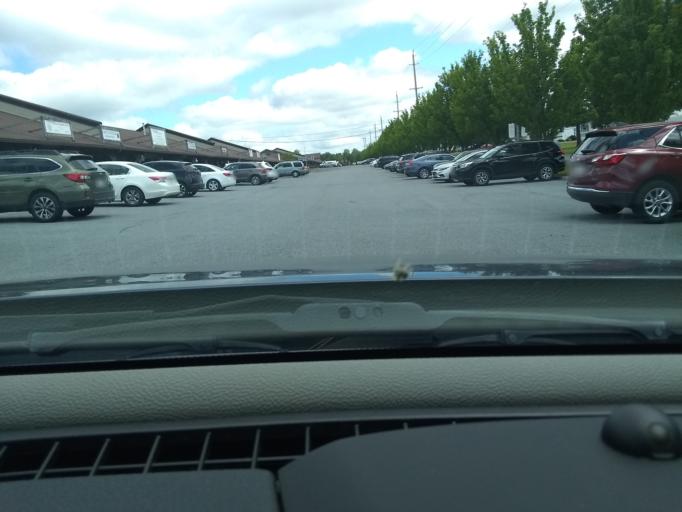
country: US
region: Pennsylvania
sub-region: Cambria County
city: Ebensburg
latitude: 40.4616
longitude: -78.7510
